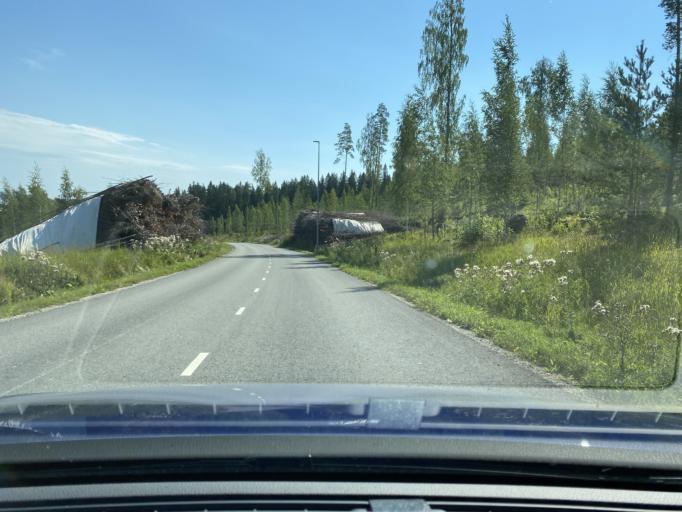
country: FI
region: Central Finland
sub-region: Jaemsae
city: Jaemsae
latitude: 61.8897
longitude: 25.3912
